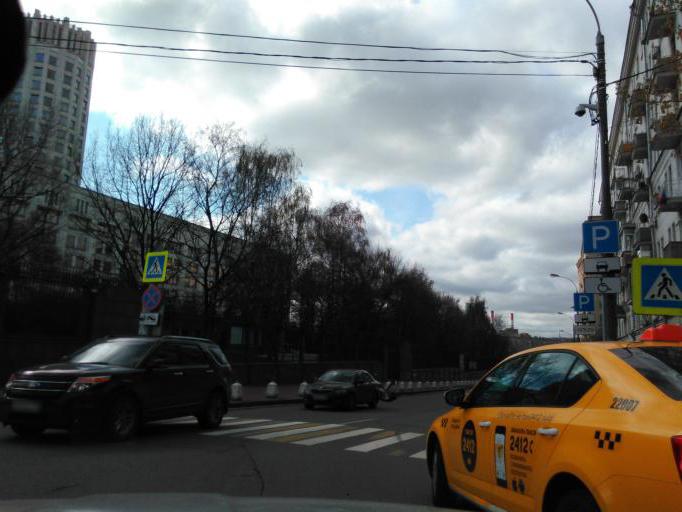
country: RU
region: Moskovskaya
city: Dorogomilovo
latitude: 55.7565
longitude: 37.5714
